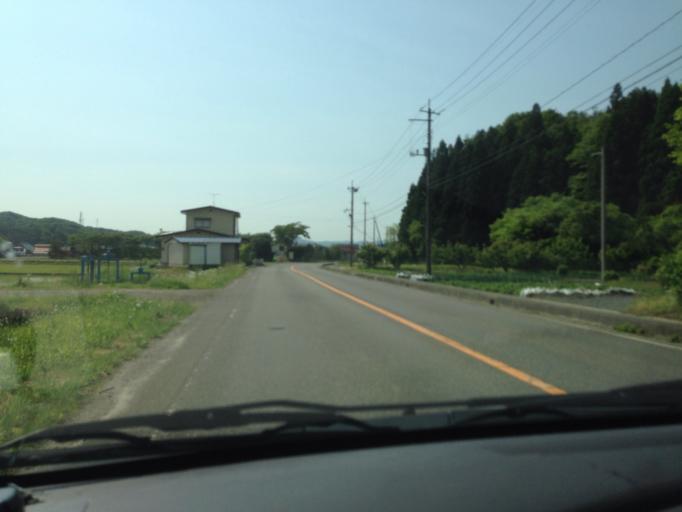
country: JP
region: Tochigi
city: Kuroiso
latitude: 37.1603
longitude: 140.1765
